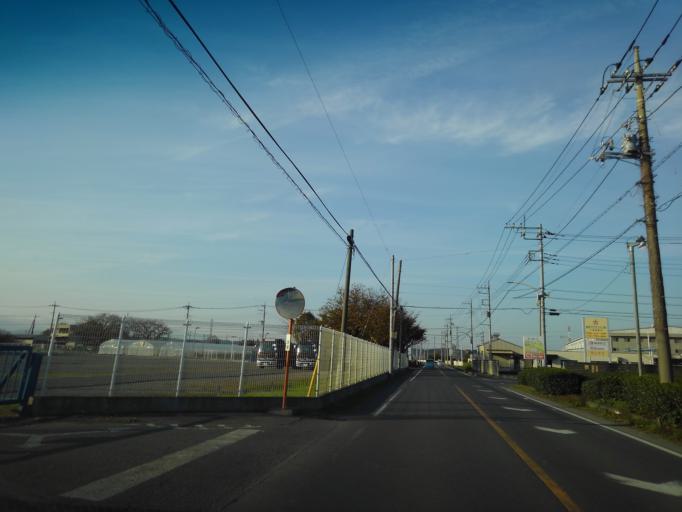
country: JP
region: Saitama
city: Hanno
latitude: 35.7996
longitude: 139.3397
